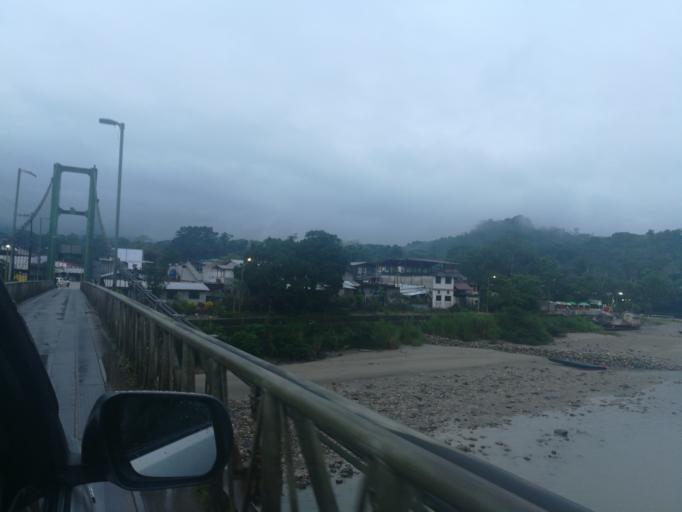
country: EC
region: Napo
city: Tena
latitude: -1.0367
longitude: -77.6669
